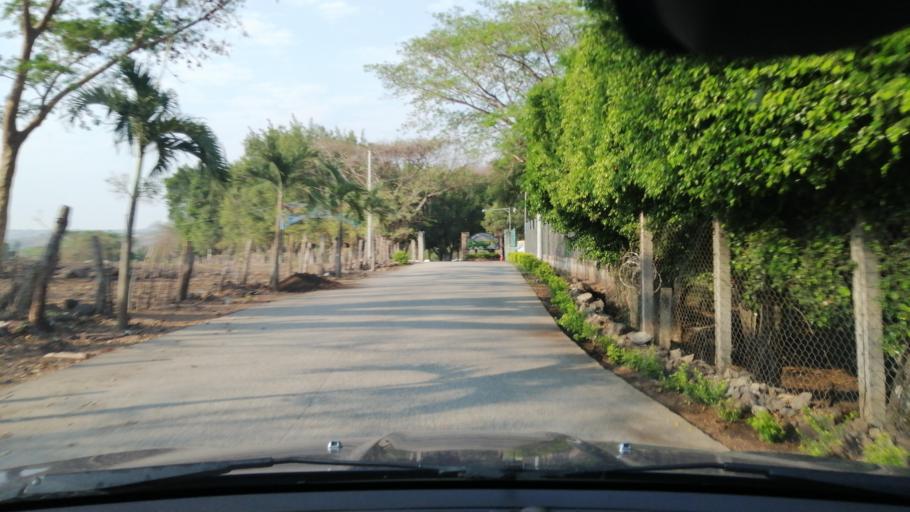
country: SV
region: Santa Ana
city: Texistepeque
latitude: 14.2193
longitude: -89.4590
